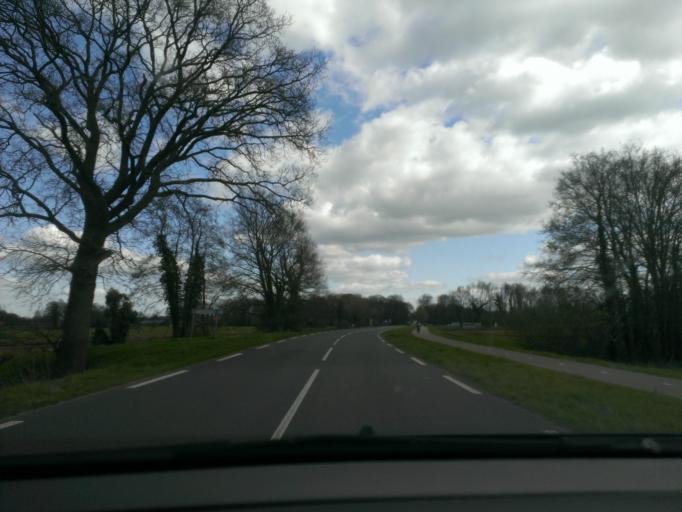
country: NL
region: Overijssel
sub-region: Gemeente Borne
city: Borne
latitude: 52.3072
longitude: 6.7163
